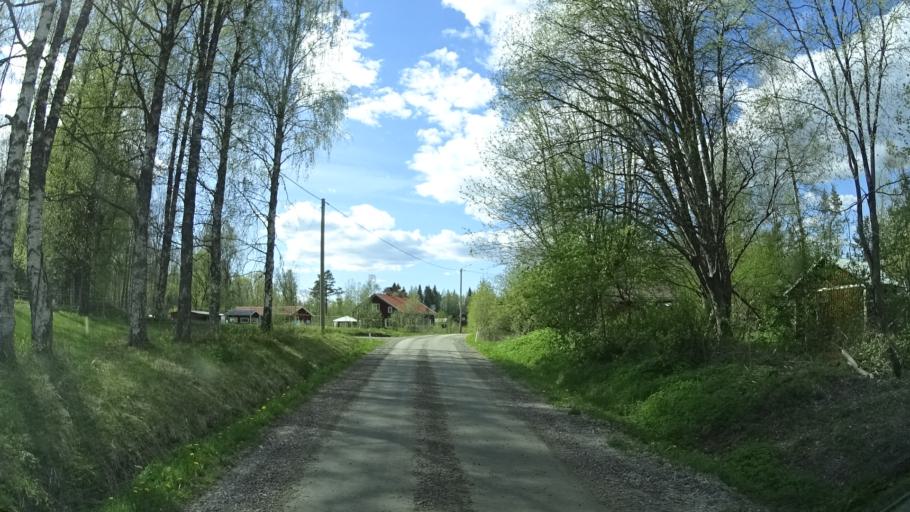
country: SE
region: OErebro
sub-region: Nora Kommun
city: As
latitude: 59.4368
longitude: 14.8582
